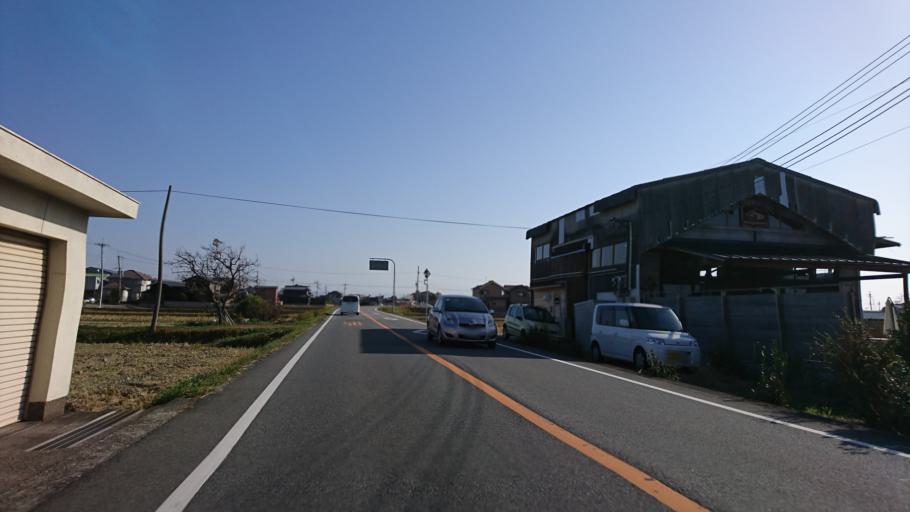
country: JP
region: Hyogo
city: Miki
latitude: 34.7608
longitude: 134.9236
